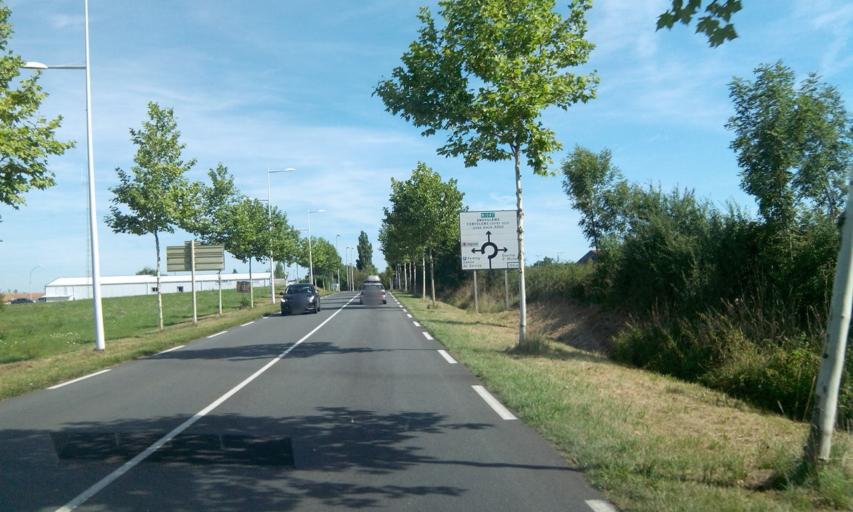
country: FR
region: Poitou-Charentes
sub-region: Departement de la Charente
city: Confolens
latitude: 46.0009
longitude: 0.6737
